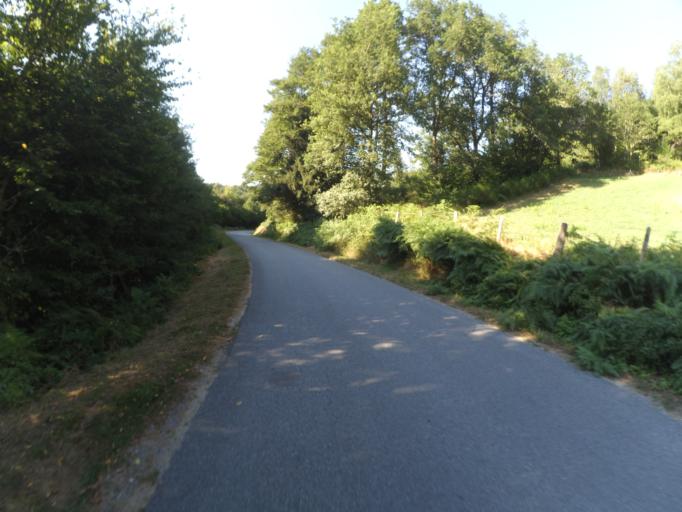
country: FR
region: Limousin
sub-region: Departement de la Correze
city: Bugeat
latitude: 45.7563
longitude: 1.9277
